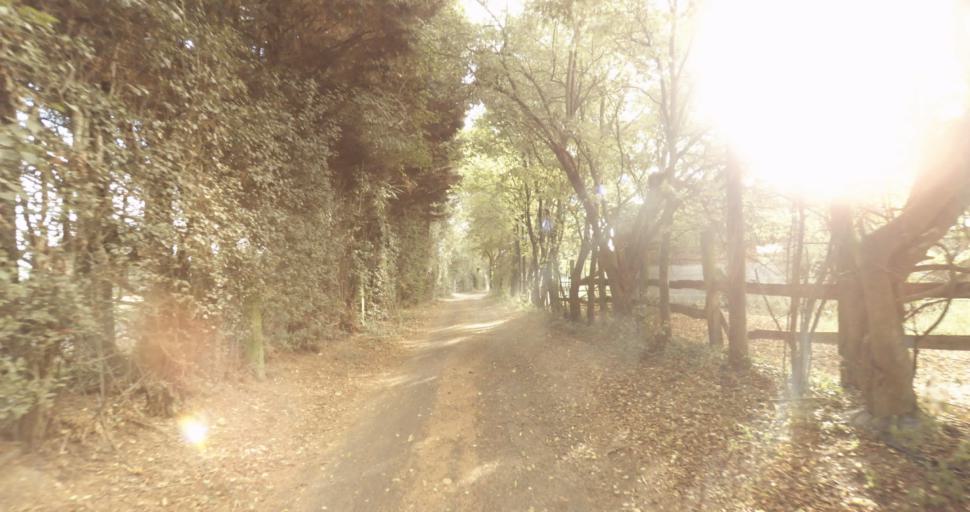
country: FR
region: Lower Normandy
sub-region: Departement de l'Orne
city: Vimoutiers
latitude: 48.9454
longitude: 0.2529
